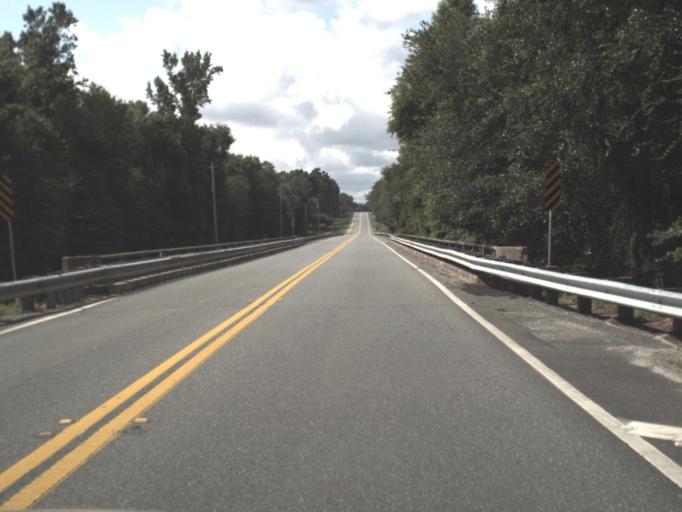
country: US
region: Florida
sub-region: Baker County
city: Macclenny
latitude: 30.3527
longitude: -82.1293
